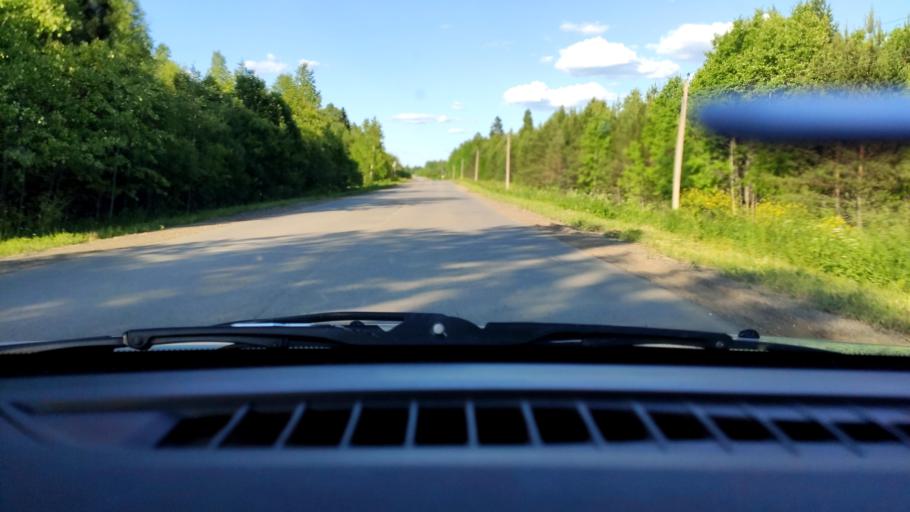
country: RU
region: Perm
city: Orda
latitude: 57.1275
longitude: 56.6900
